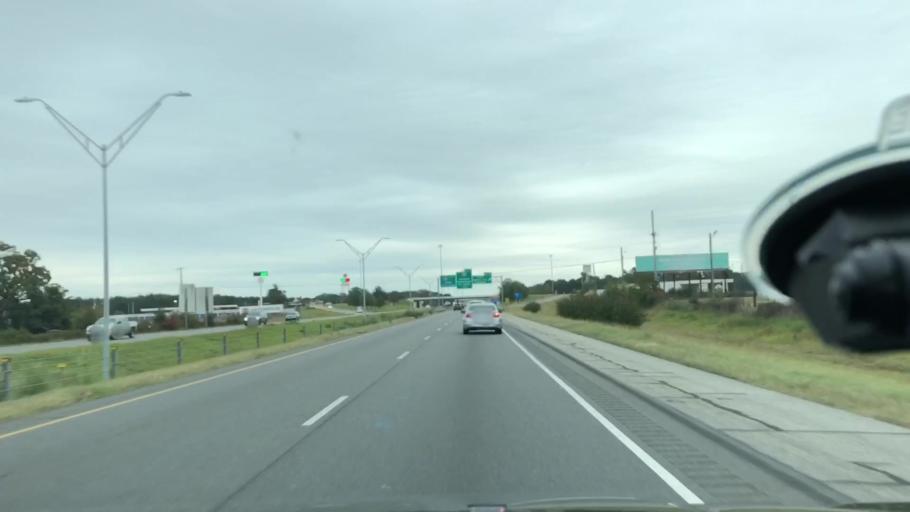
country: US
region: Arkansas
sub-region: Miller County
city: Texarkana
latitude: 33.4745
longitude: -94.0133
